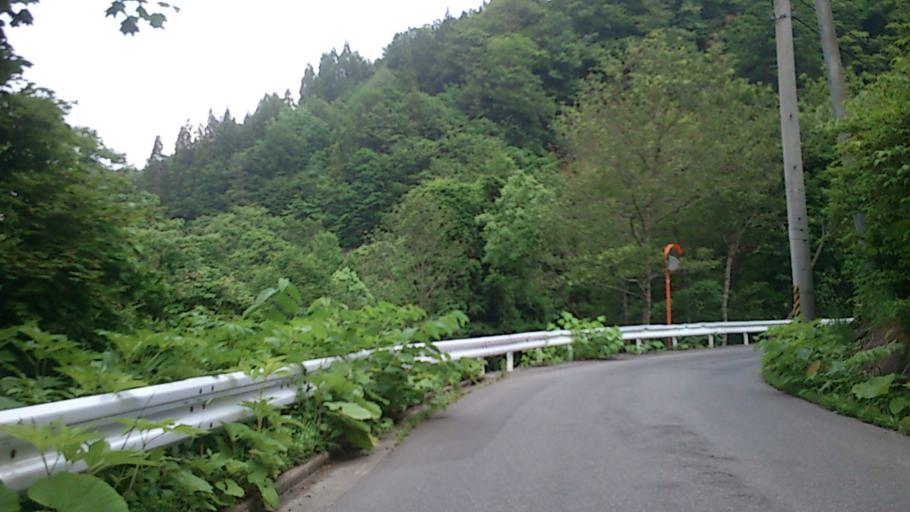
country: JP
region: Aomori
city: Hirosaki
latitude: 40.5176
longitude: 140.1796
